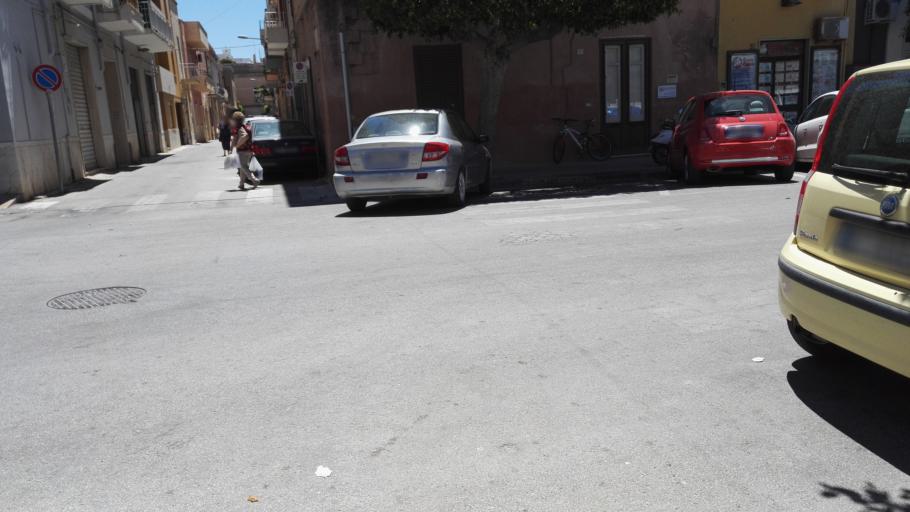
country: IT
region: Sicily
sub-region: Trapani
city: Marsala
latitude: 37.7964
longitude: 12.4381
